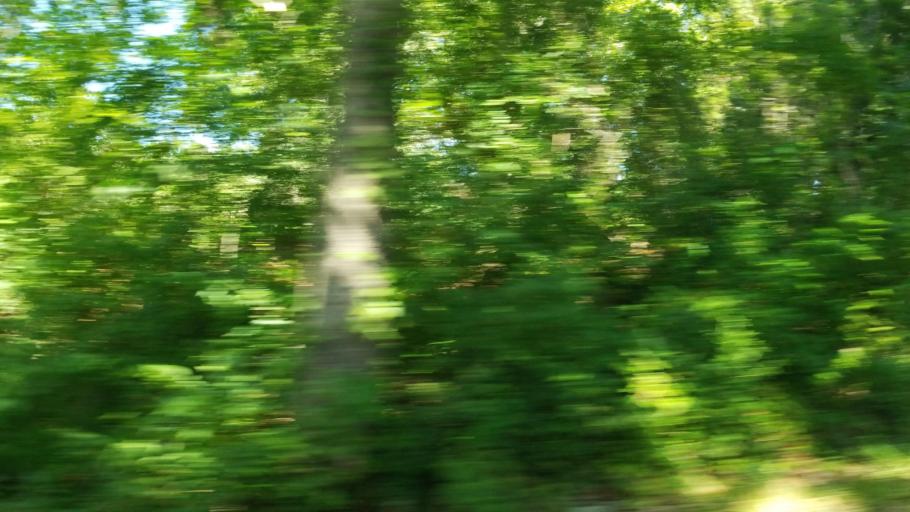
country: US
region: Illinois
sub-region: Williamson County
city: Johnston City
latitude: 37.7848
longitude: -88.8210
